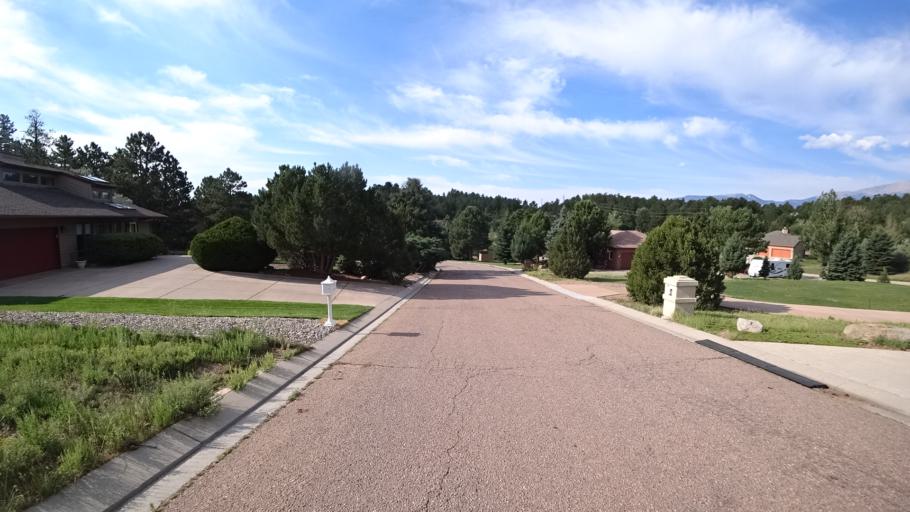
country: US
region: Colorado
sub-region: El Paso County
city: Air Force Academy
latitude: 38.9386
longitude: -104.8279
